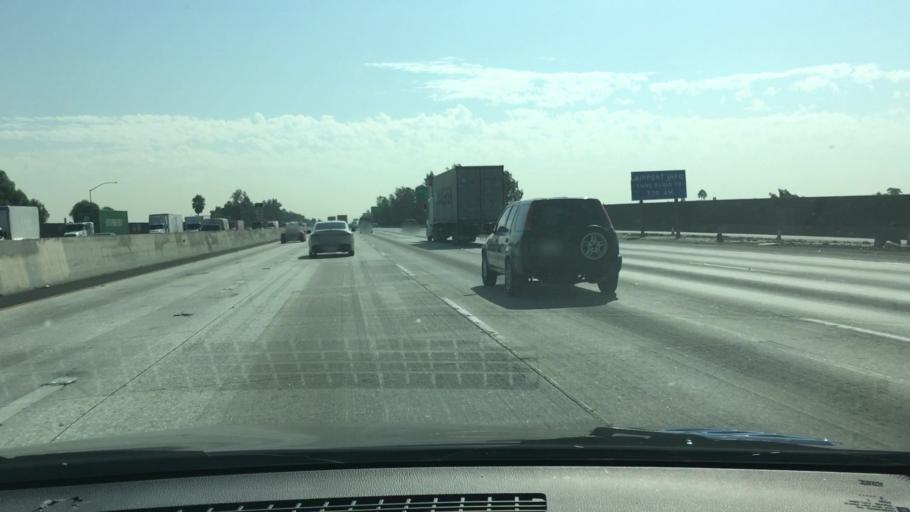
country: US
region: California
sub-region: San Bernardino County
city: Chino
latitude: 34.0303
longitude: -117.6659
